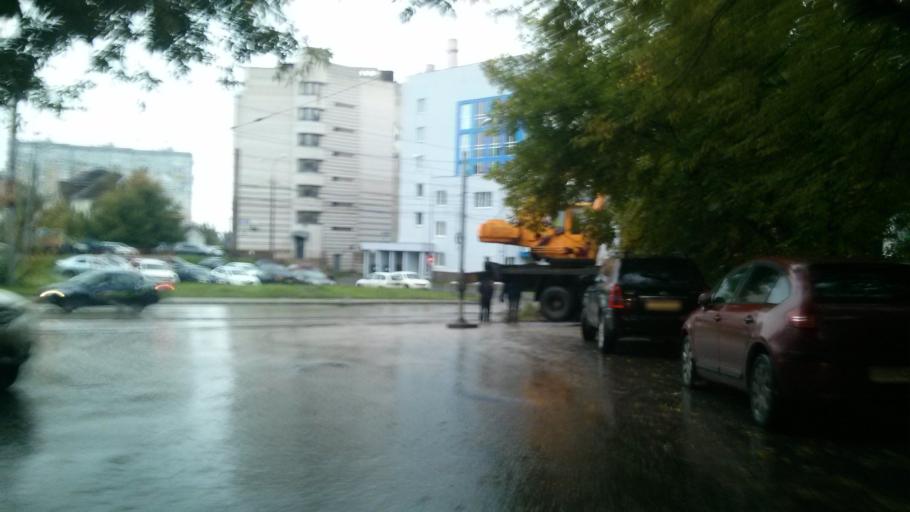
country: RU
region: Nizjnij Novgorod
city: Nizhniy Novgorod
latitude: 56.3032
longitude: 43.9887
